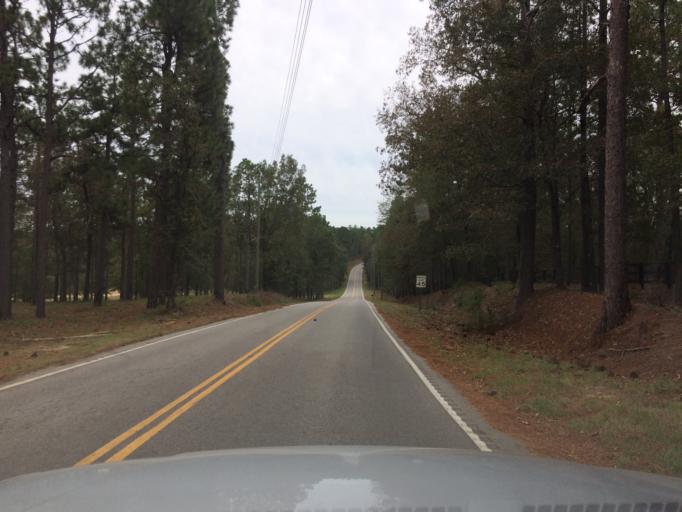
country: US
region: South Carolina
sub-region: Aiken County
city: New Ellenton
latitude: 33.4764
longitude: -81.6569
